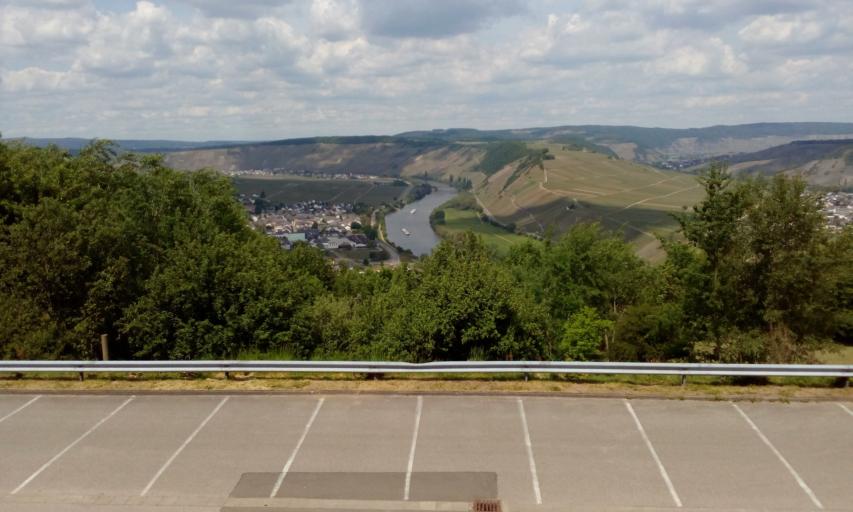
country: DE
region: Rheinland-Pfalz
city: Leiwen
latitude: 49.8098
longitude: 6.8906
